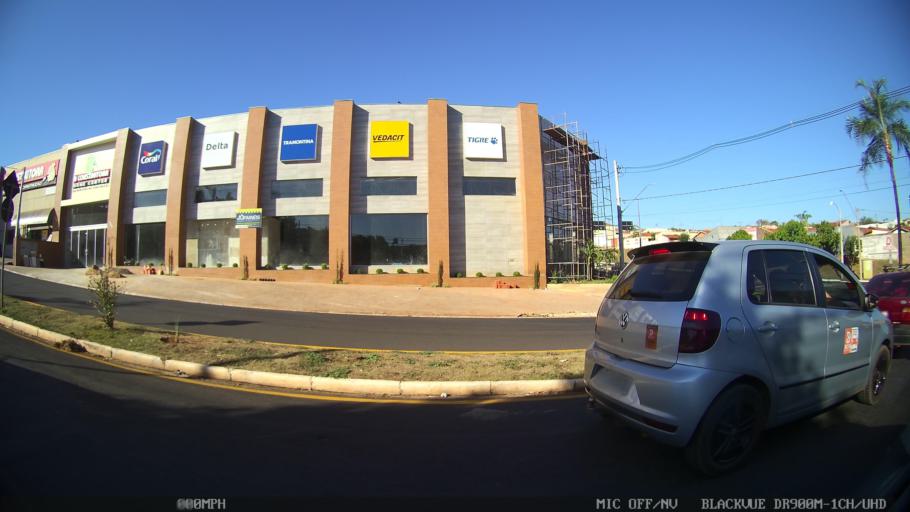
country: BR
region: Sao Paulo
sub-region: Olimpia
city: Olimpia
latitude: -20.7391
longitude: -48.9034
